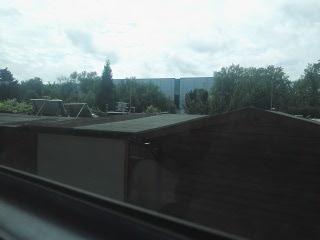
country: DE
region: Bavaria
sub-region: Swabia
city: Augsburg
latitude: 48.3867
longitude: 10.8988
